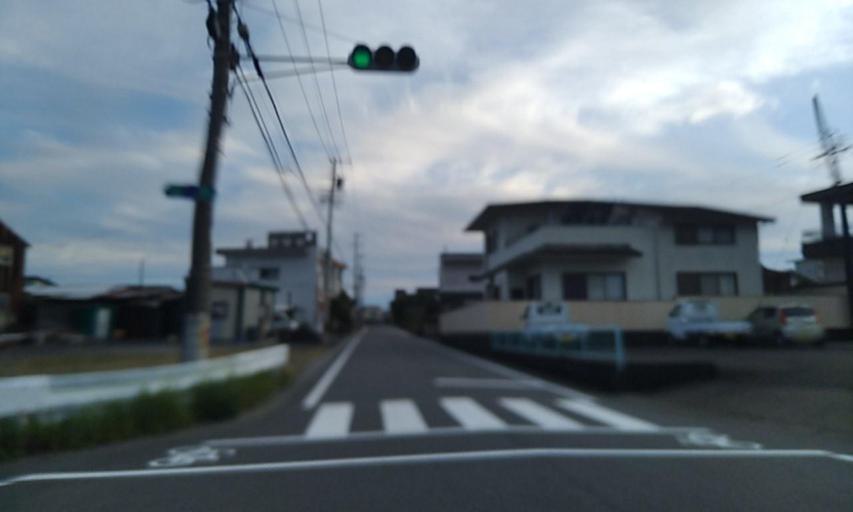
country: JP
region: Mie
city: Toba
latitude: 34.2848
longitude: 136.8854
